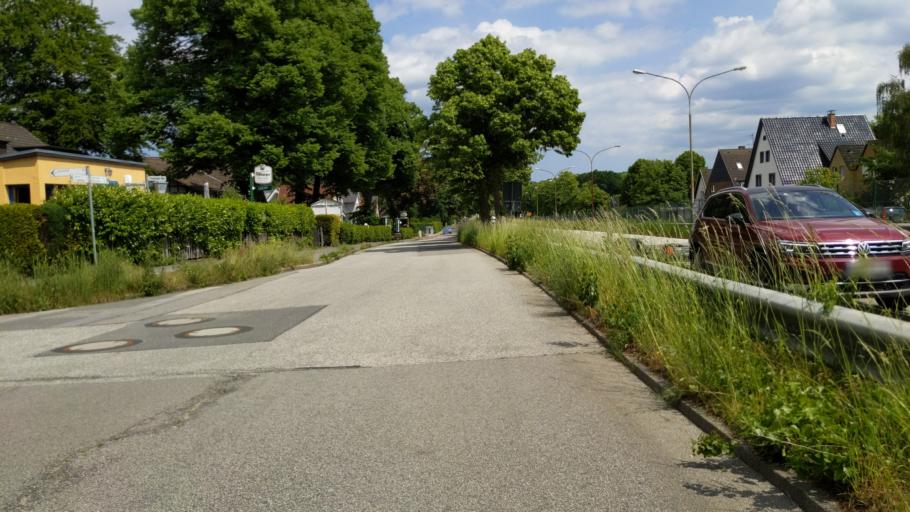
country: DE
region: Schleswig-Holstein
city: Luebeck
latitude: 53.8865
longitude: 10.7129
